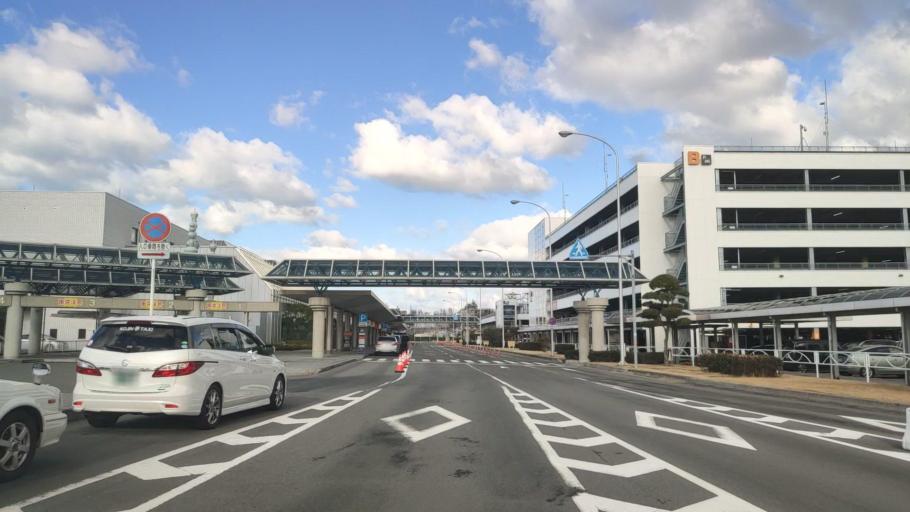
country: JP
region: Ehime
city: Masaki-cho
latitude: 33.8284
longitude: 132.7057
